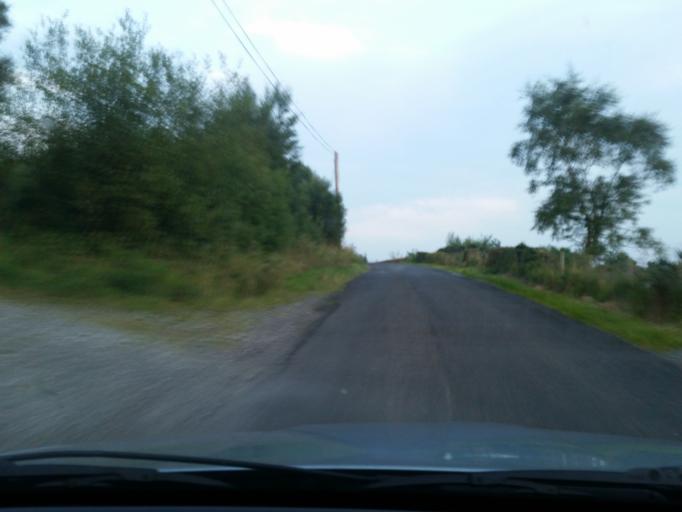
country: GB
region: Northern Ireland
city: Fivemiletown
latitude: 54.3212
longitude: -7.2961
